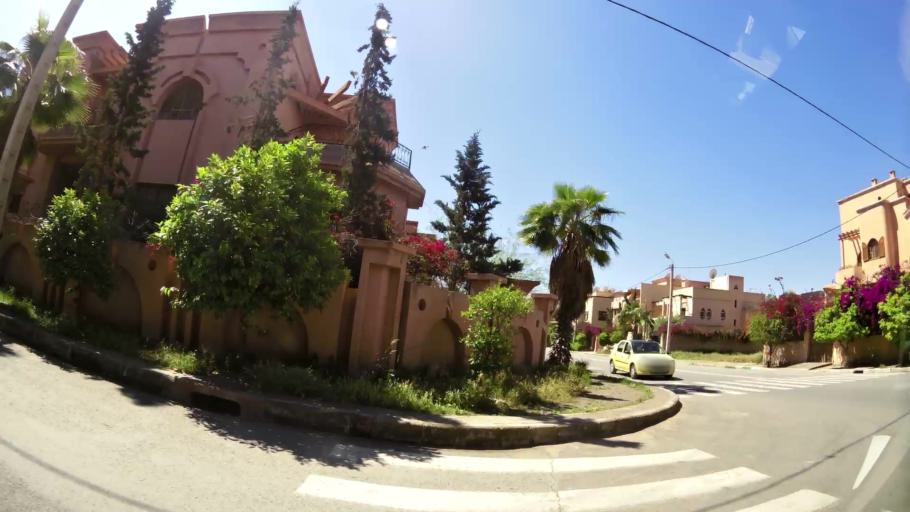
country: MA
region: Marrakech-Tensift-Al Haouz
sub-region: Marrakech
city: Marrakesh
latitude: 31.6379
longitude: -8.0664
